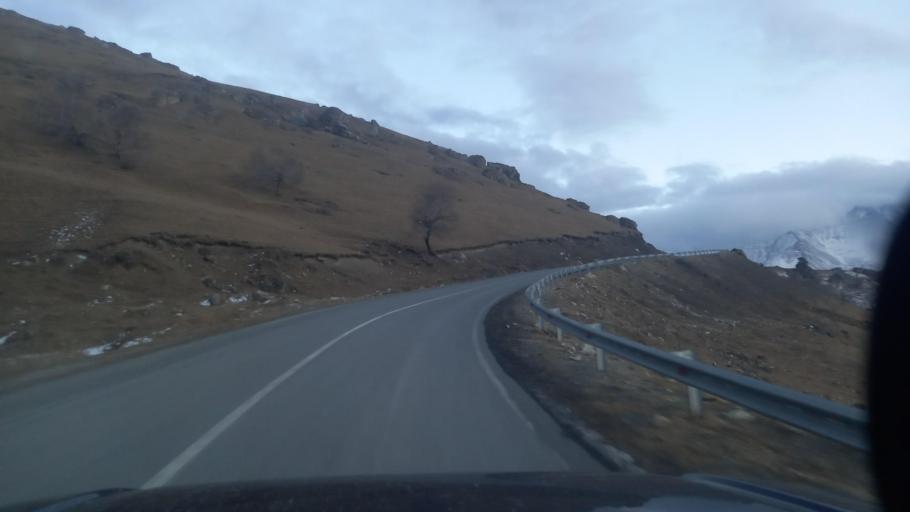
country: RU
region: Ingushetiya
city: Dzhayrakh
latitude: 42.8240
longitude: 44.8274
